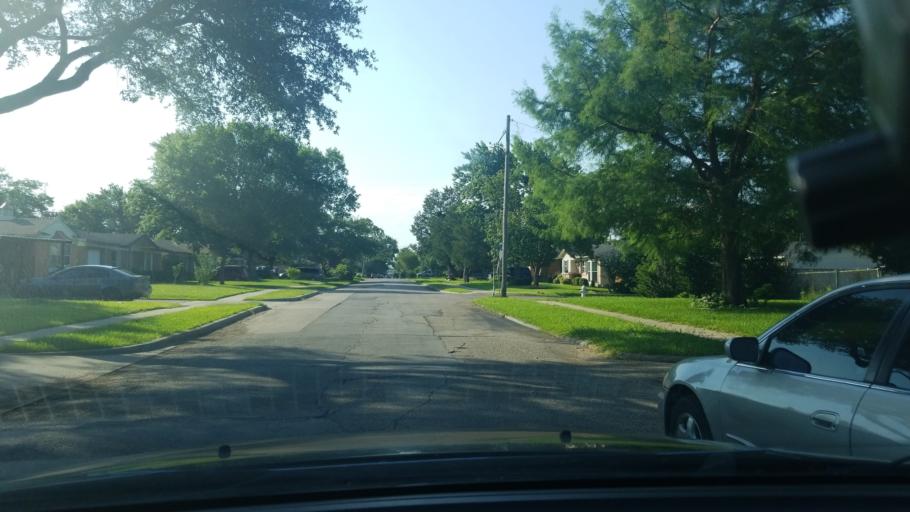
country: US
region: Texas
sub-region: Dallas County
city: Mesquite
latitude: 32.8148
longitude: -96.6395
